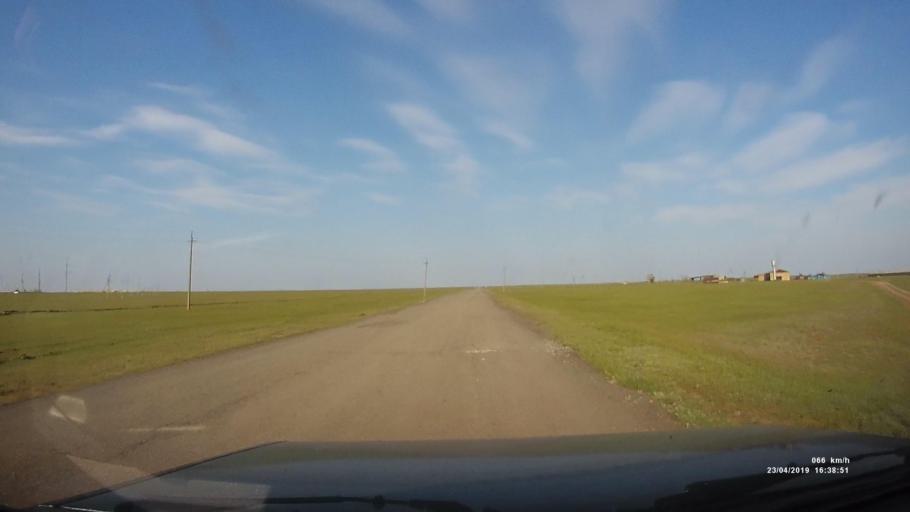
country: RU
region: Kalmykiya
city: Priyutnoye
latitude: 46.3373
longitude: 43.1586
